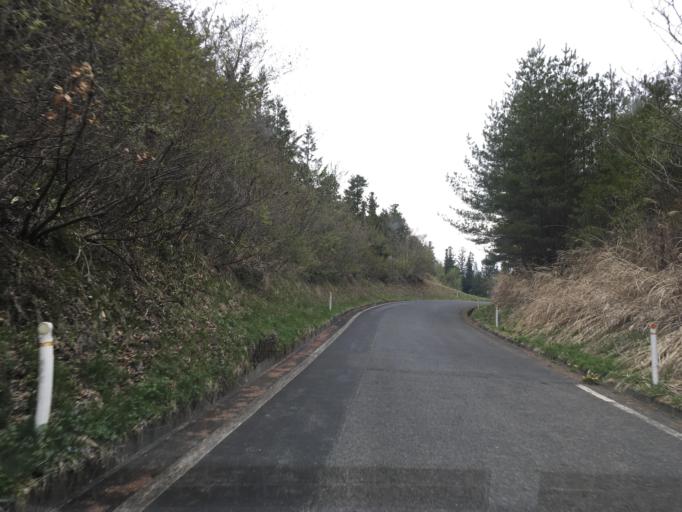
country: JP
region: Iwate
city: Ichinoseki
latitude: 38.8436
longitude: 141.3334
